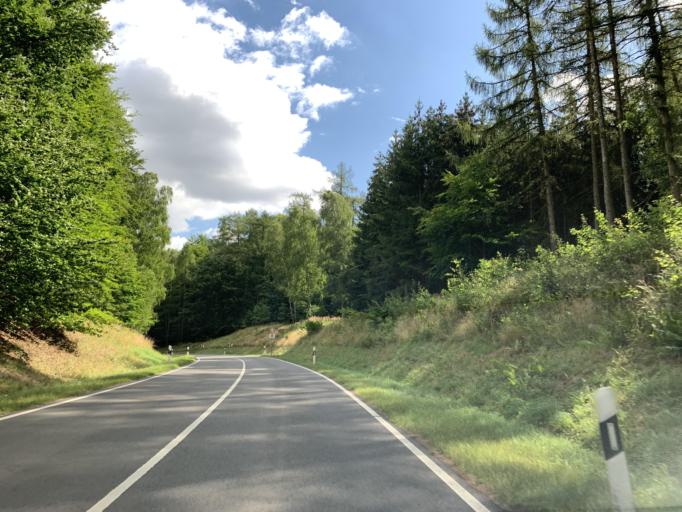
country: DE
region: Mecklenburg-Vorpommern
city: Wustrow
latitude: 53.4190
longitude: 13.1786
